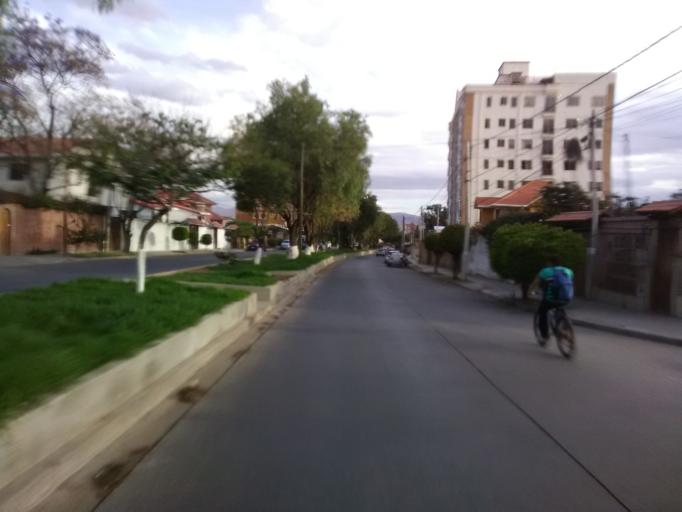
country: BO
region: Cochabamba
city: Cochabamba
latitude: -17.3676
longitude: -66.1713
